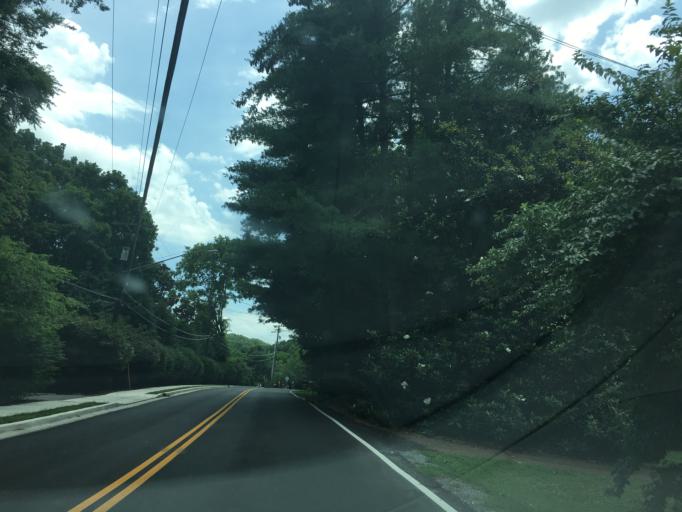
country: US
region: Tennessee
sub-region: Davidson County
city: Oak Hill
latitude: 36.0991
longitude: -86.8095
